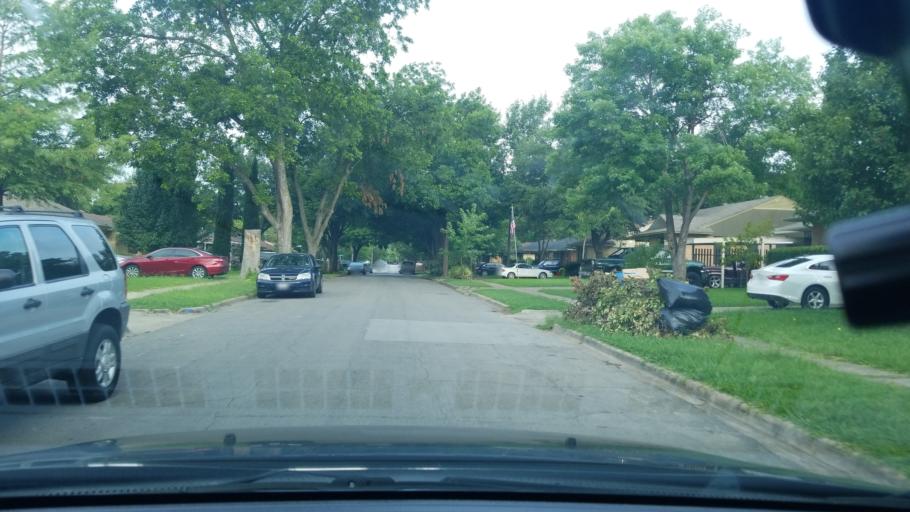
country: US
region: Texas
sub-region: Dallas County
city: Garland
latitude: 32.8304
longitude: -96.6588
